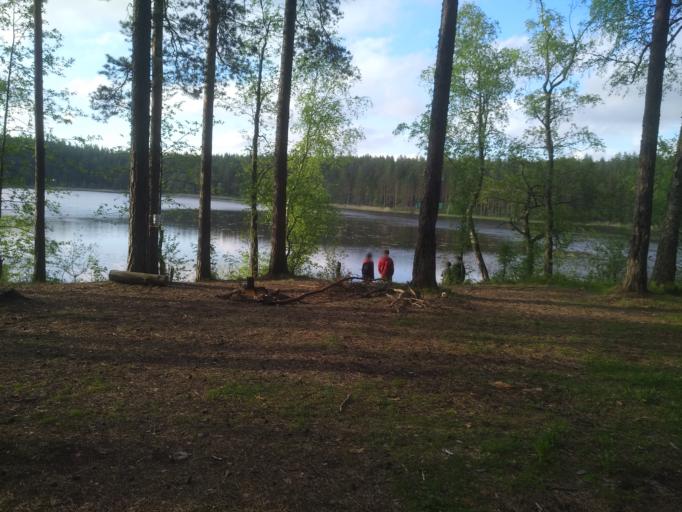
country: RU
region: Leningrad
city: Michurinskoye
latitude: 60.6021
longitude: 29.8815
